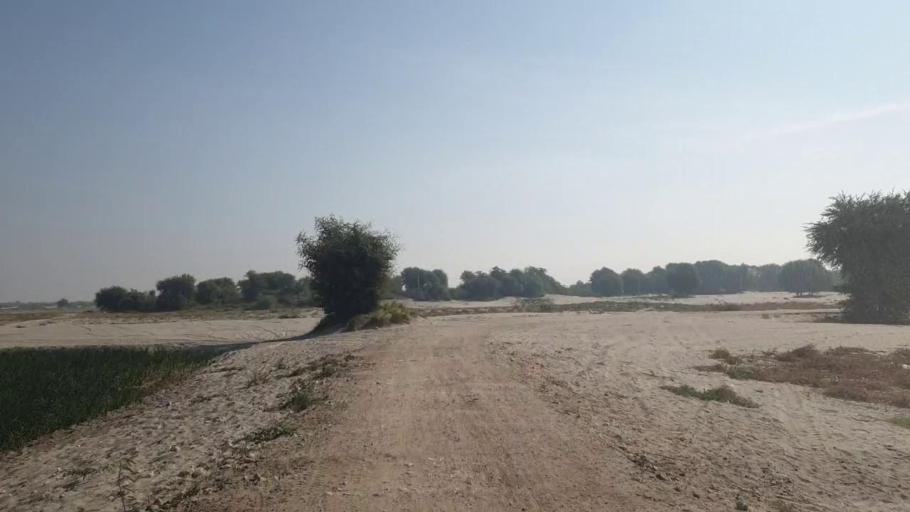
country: PK
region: Sindh
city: Matiari
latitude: 25.6743
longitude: 68.3620
